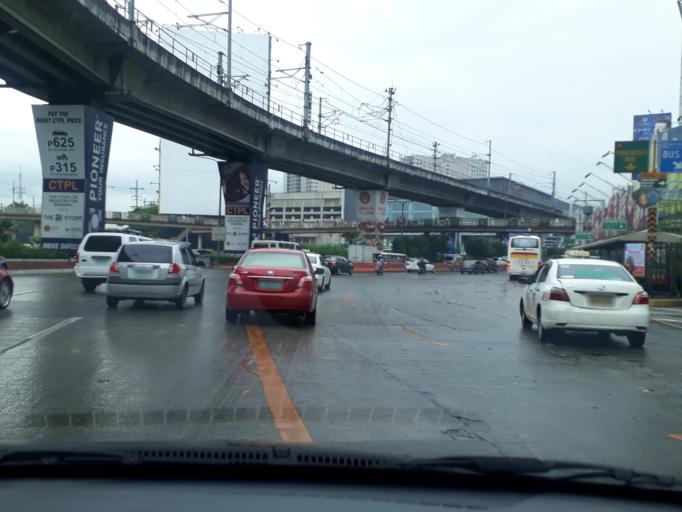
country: PH
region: Calabarzon
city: Bagong Pagasa
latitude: 14.6556
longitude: 121.0296
